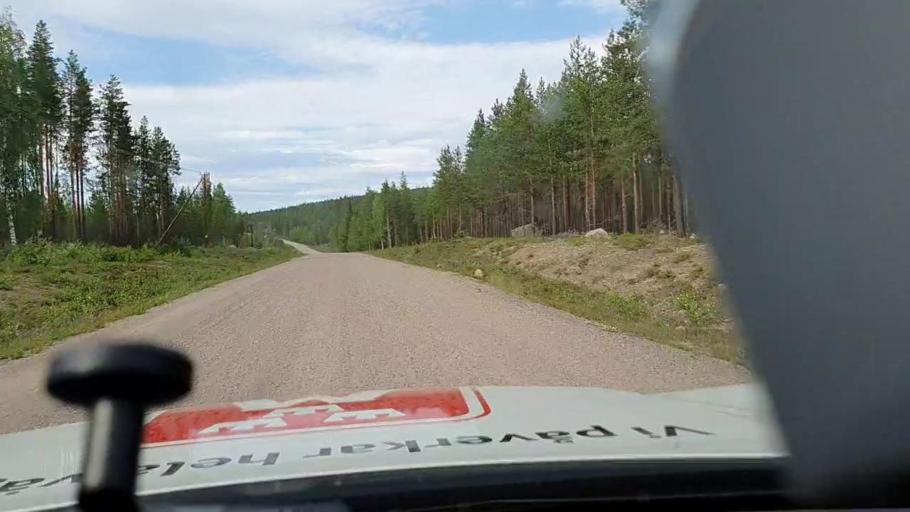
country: SE
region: Norrbotten
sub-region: Alvsbyns Kommun
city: AElvsbyn
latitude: 66.1250
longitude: 20.9953
